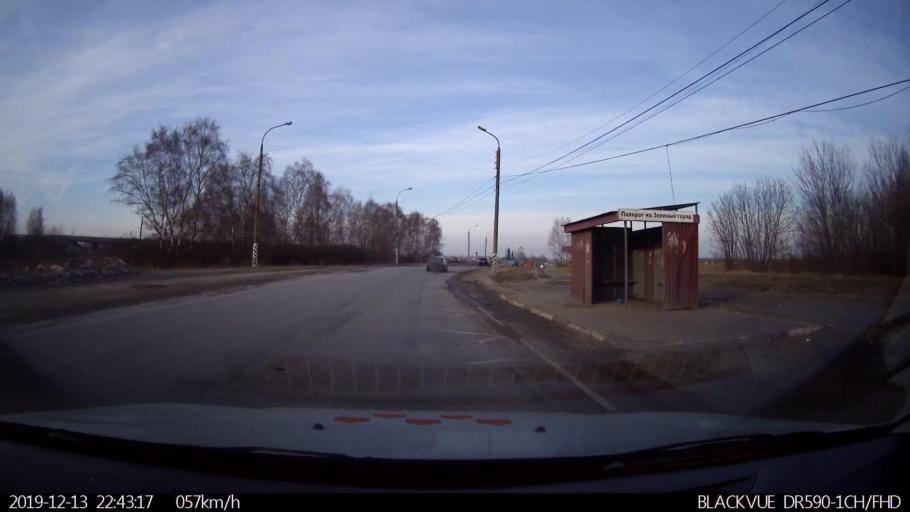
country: RU
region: Nizjnij Novgorod
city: Afonino
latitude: 56.1952
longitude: 44.1250
